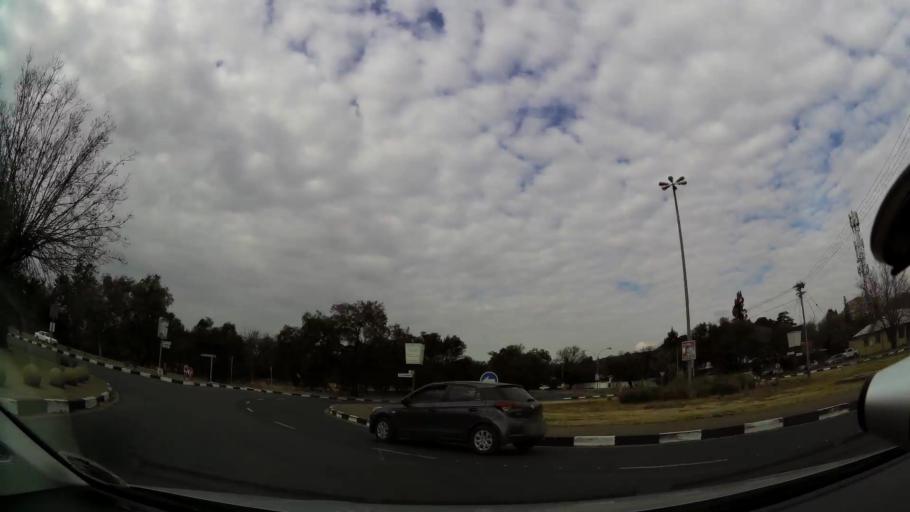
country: ZA
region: Orange Free State
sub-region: Mangaung Metropolitan Municipality
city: Bloemfontein
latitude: -29.0883
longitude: 26.2299
